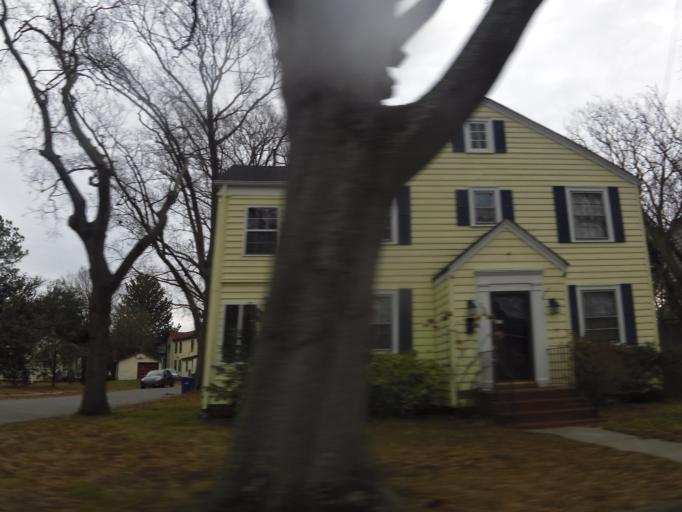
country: US
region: Virginia
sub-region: City of Portsmouth
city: Portsmouth
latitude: 36.8431
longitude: -76.3238
